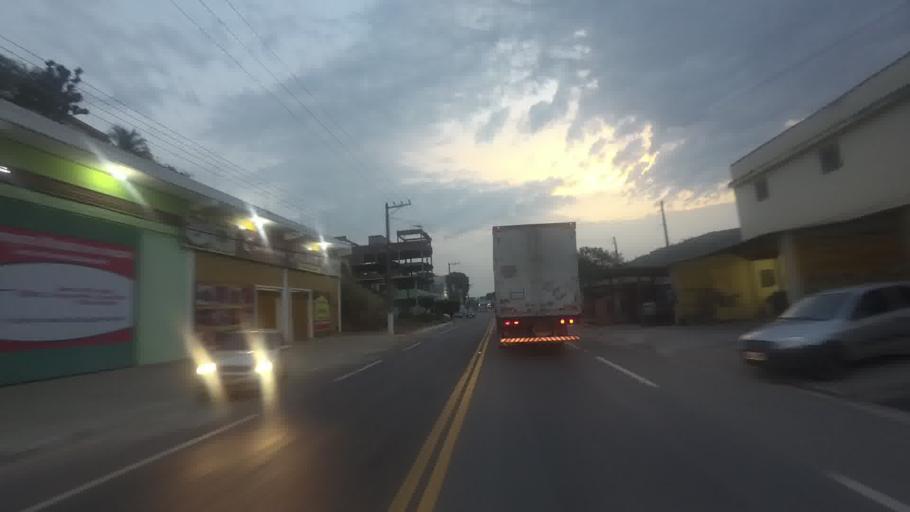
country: BR
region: Minas Gerais
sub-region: Alem Paraiba
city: Alem Paraiba
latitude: -21.8898
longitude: -42.7042
